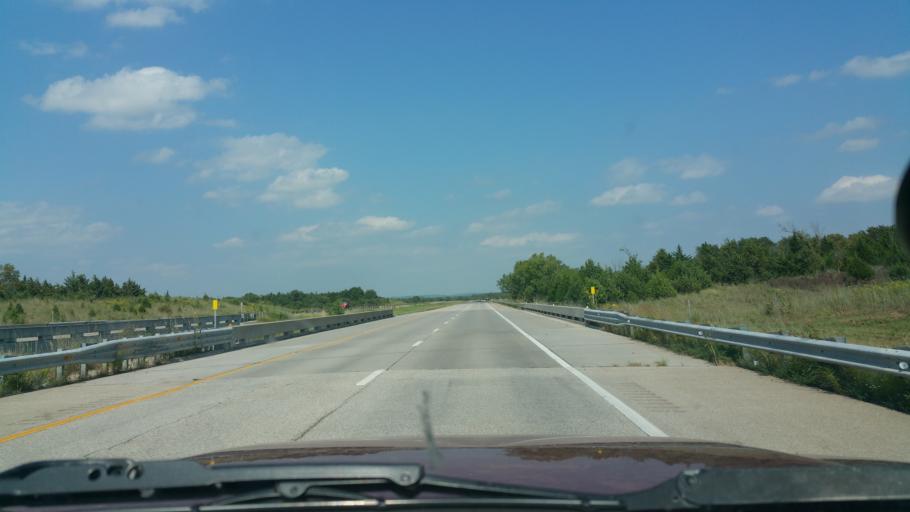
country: US
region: Kansas
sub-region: Riley County
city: Ogden
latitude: 39.0726
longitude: -96.7385
